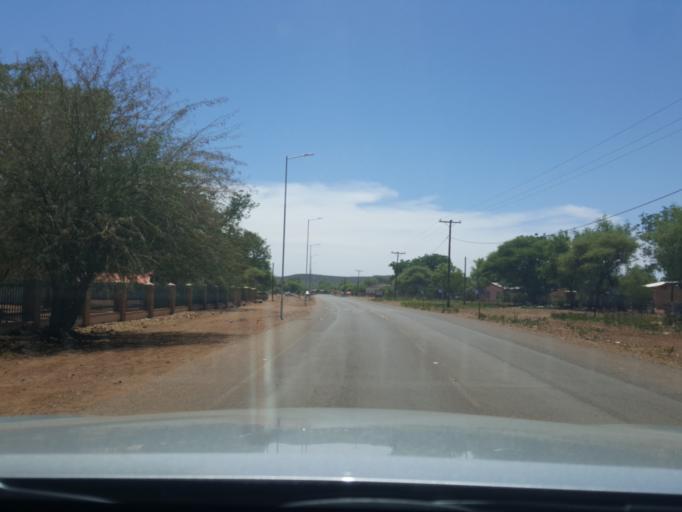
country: BW
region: South East
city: Ramotswa
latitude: -24.8683
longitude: 25.8719
